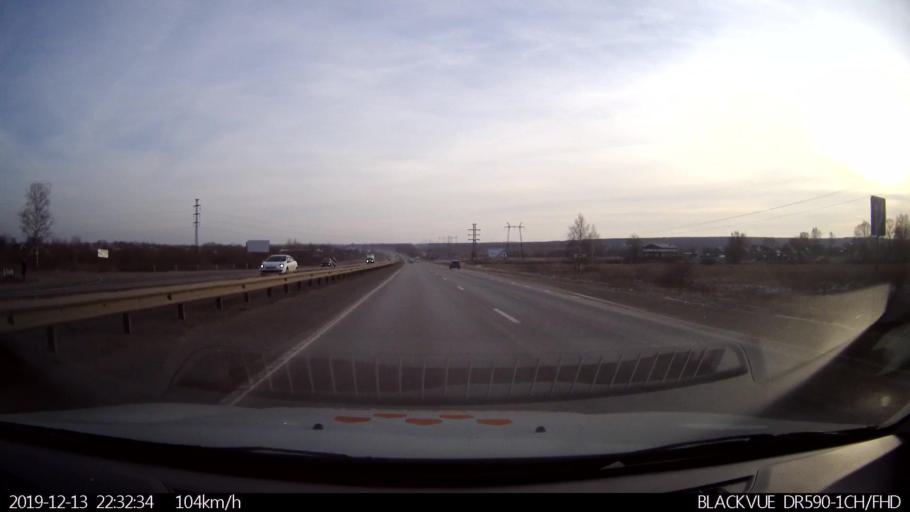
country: RU
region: Nizjnij Novgorod
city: Afonino
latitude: 56.2042
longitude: 44.0941
